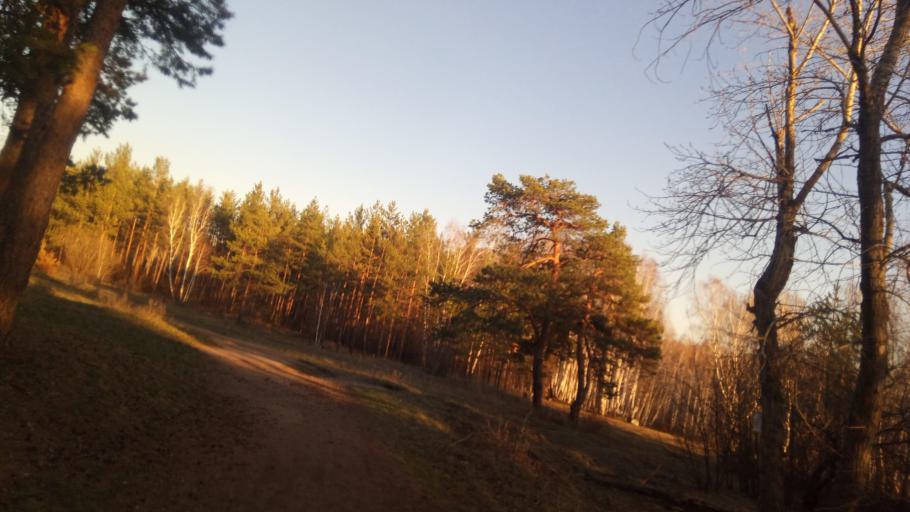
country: RU
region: Chelyabinsk
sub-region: Gorod Chelyabinsk
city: Chelyabinsk
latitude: 55.1594
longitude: 61.3240
